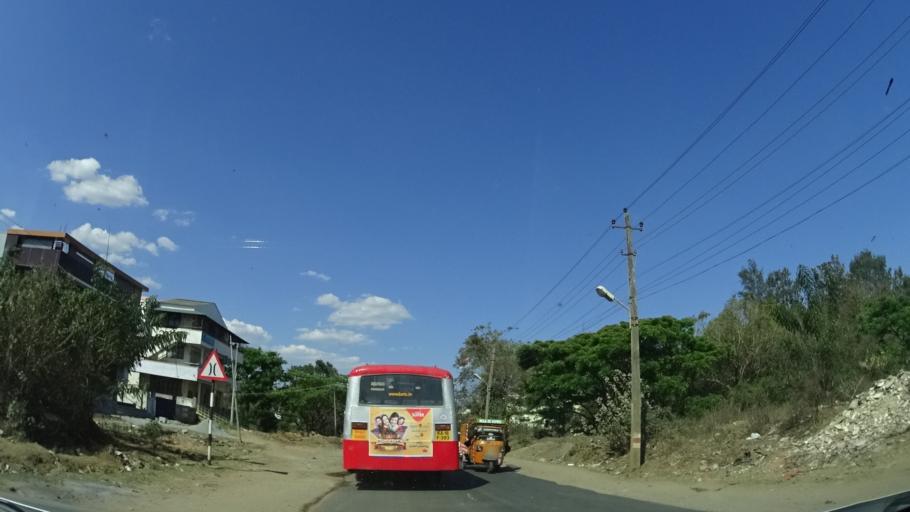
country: IN
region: Karnataka
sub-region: Chikmagalur
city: Chikmagalur
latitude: 13.3064
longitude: 75.7667
